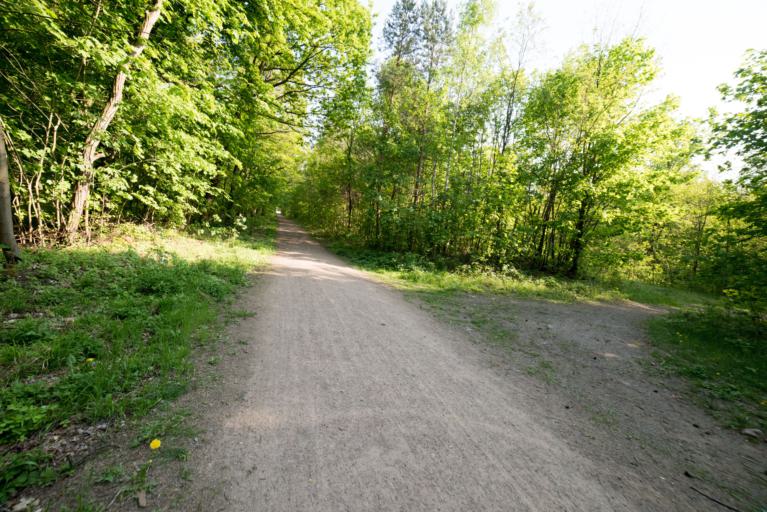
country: DE
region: Saxony
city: Albertstadt
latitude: 51.0777
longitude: 13.7799
